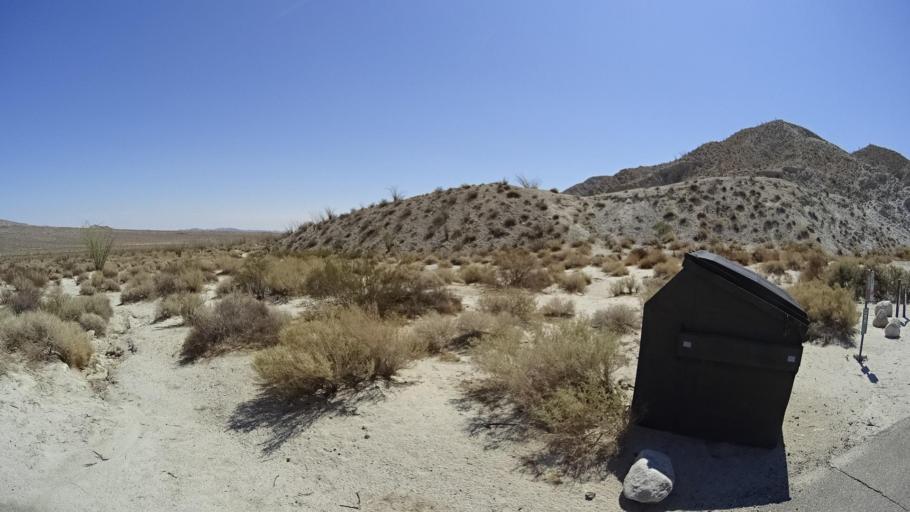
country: US
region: California
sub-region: San Diego County
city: Pine Valley
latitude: 32.9494
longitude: -116.3012
